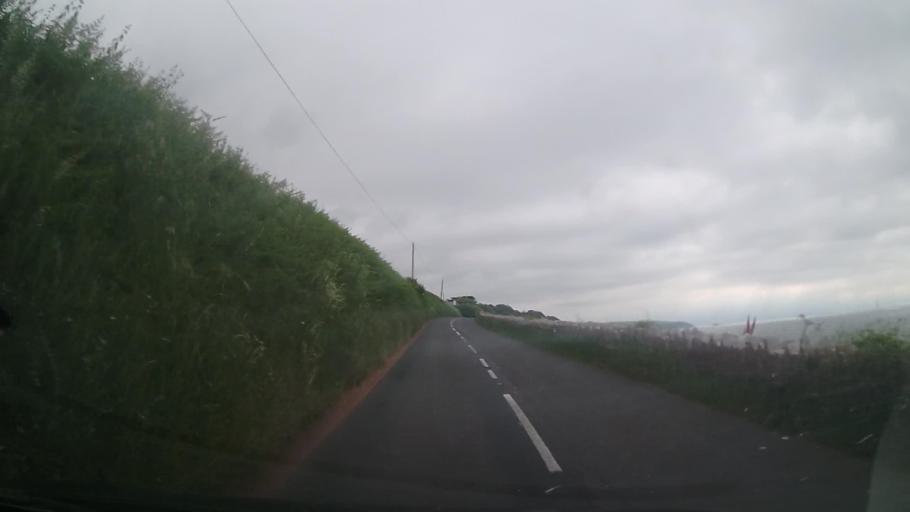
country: GB
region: England
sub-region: Devon
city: Dartmouth
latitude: 50.3010
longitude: -3.6376
